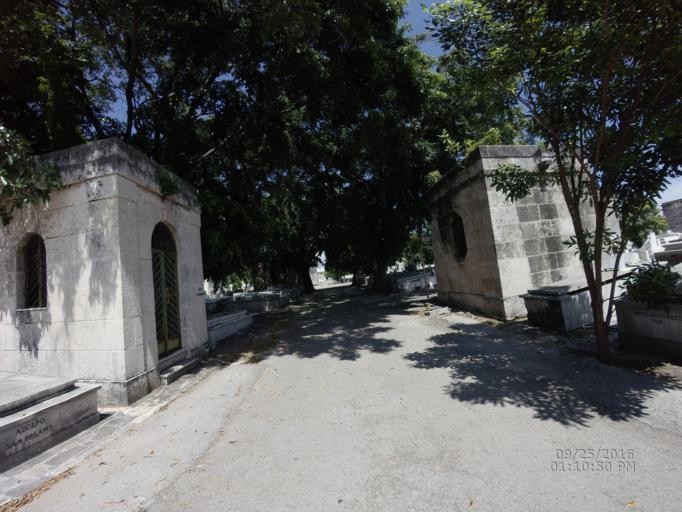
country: CU
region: La Habana
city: Havana
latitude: 23.1227
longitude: -82.4007
